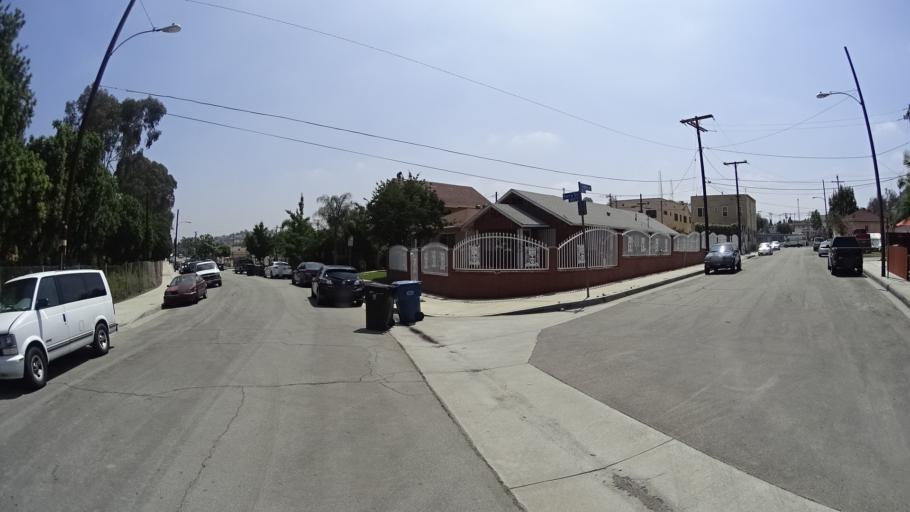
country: US
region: California
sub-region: Los Angeles County
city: Belvedere
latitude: 34.0569
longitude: -118.1803
